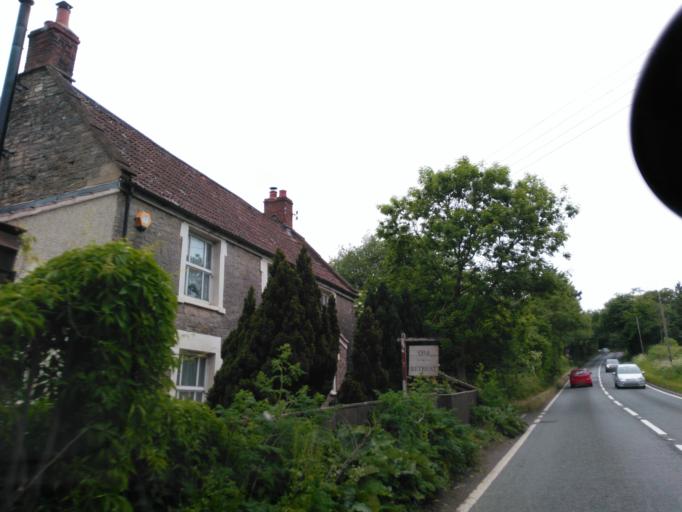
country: GB
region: England
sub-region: Somerset
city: Shepton Mallet
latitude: 51.1631
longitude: -2.5956
